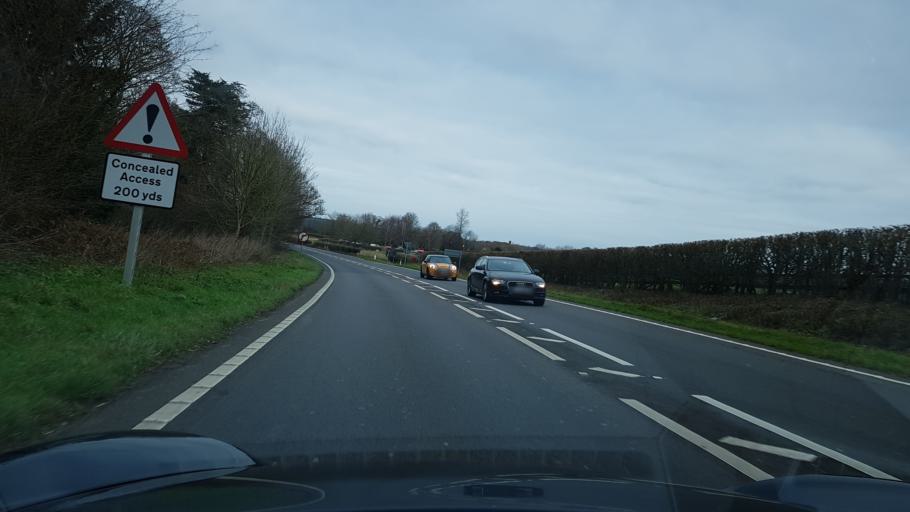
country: GB
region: England
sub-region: Dorset
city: Lytchett Matravers
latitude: 50.7780
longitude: -2.1354
